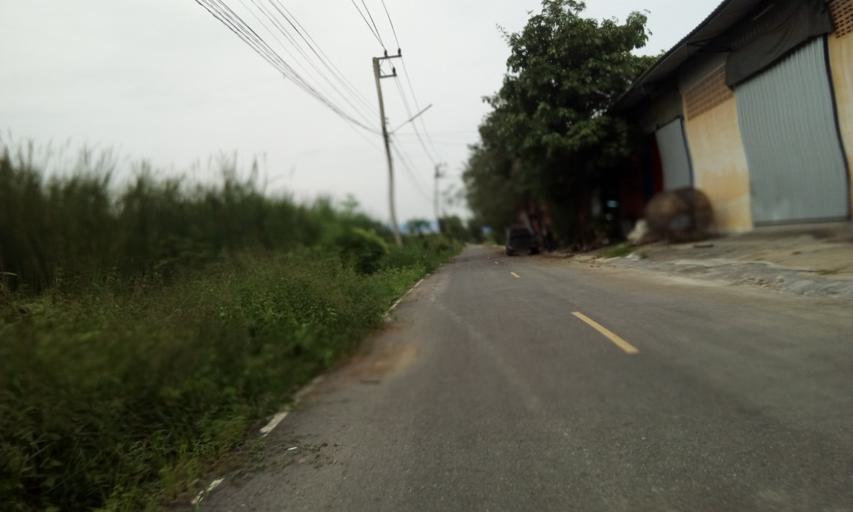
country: TH
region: Pathum Thani
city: Nong Suea
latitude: 14.0617
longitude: 100.8437
